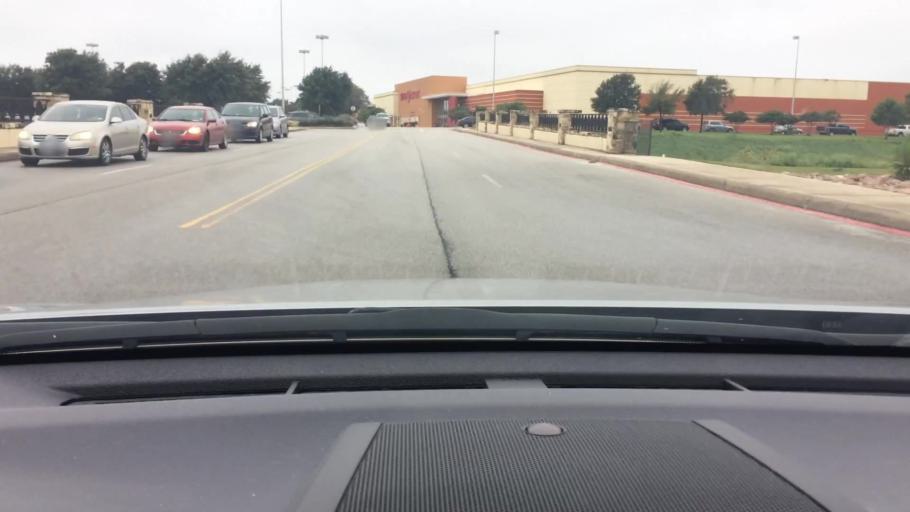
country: US
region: Texas
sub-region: Bexar County
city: Helotes
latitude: 29.4944
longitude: -98.7085
